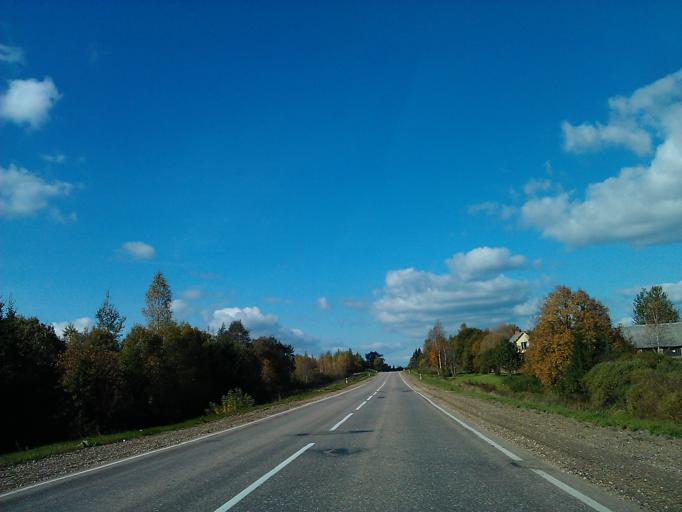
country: LV
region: Varkava
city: Vecvarkava
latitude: 56.1570
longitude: 26.3397
